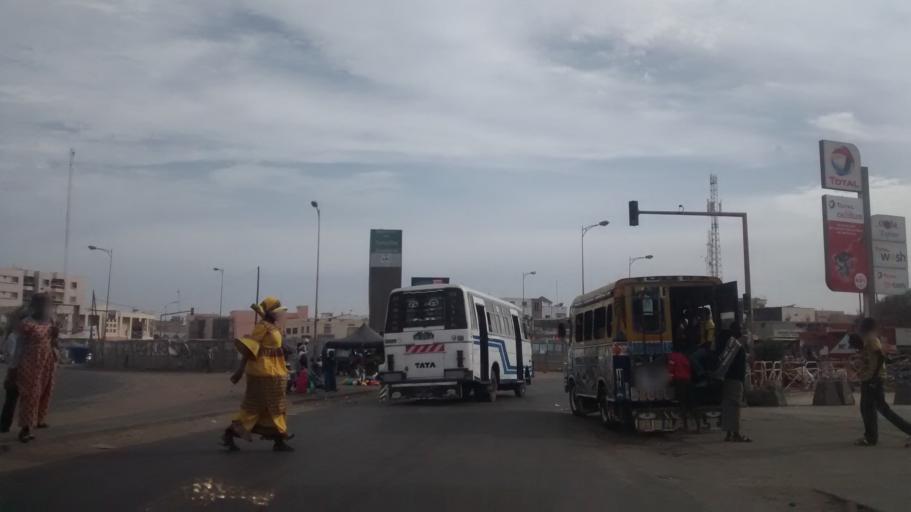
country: SN
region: Dakar
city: Pikine
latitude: 14.7563
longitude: -17.4294
